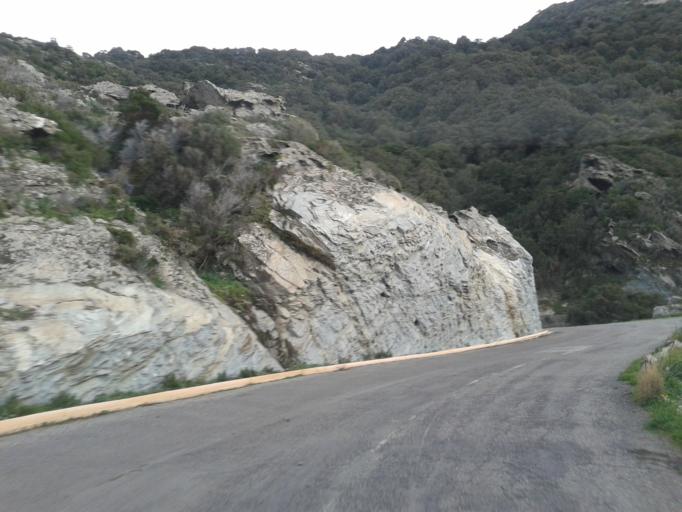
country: FR
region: Corsica
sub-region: Departement de la Haute-Corse
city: Brando
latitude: 42.9000
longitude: 9.3300
